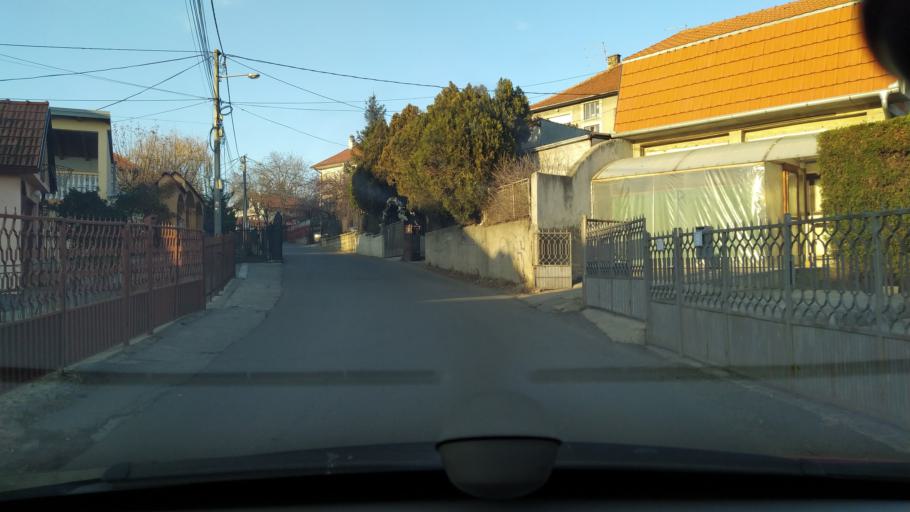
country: RS
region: Central Serbia
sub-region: Belgrade
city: Zvezdara
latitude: 44.7645
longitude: 20.5616
